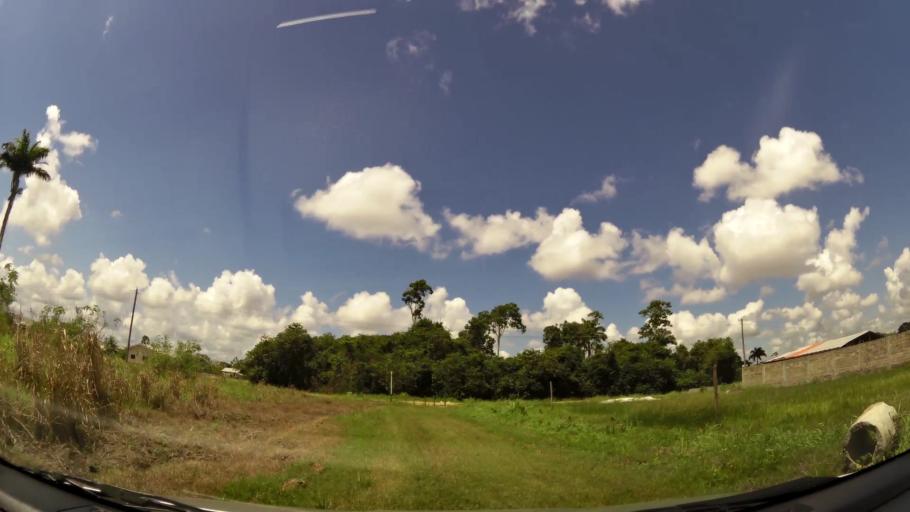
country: SR
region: Paramaribo
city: Paramaribo
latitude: 5.8618
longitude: -55.1572
